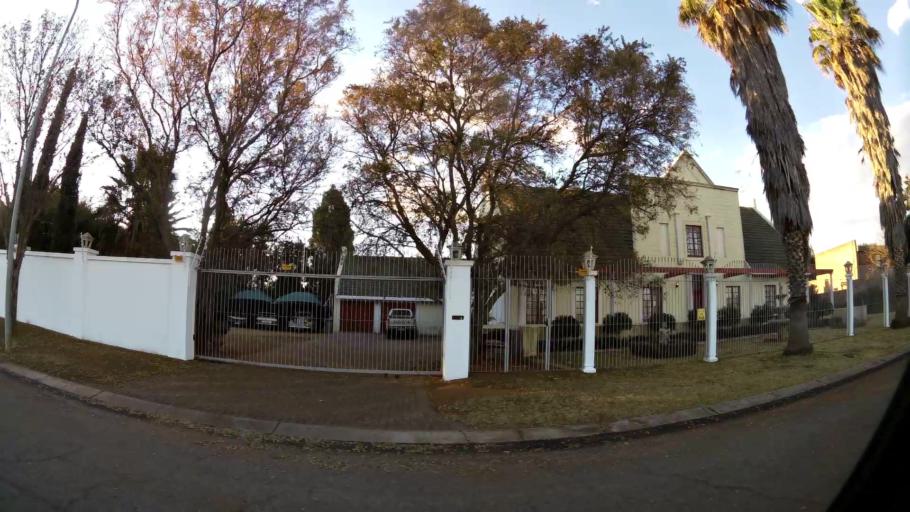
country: ZA
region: North-West
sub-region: Dr Kenneth Kaunda District Municipality
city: Potchefstroom
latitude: -26.6805
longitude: 27.1075
